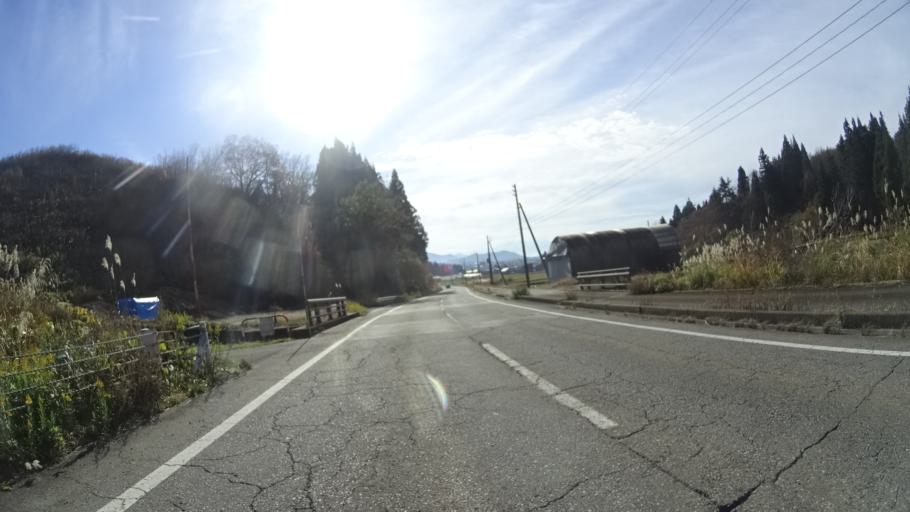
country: JP
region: Niigata
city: Muikamachi
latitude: 37.1888
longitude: 138.9815
